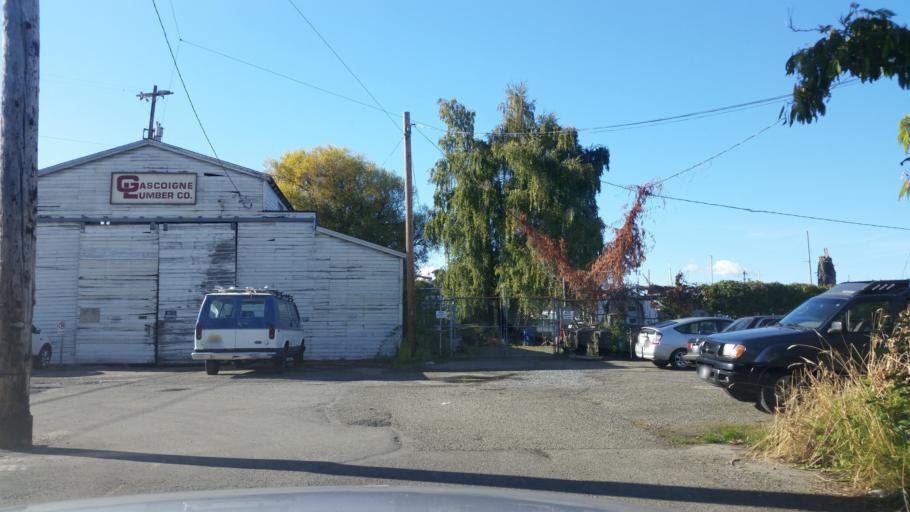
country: US
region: Washington
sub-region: King County
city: Seattle
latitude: 47.6526
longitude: -122.3639
